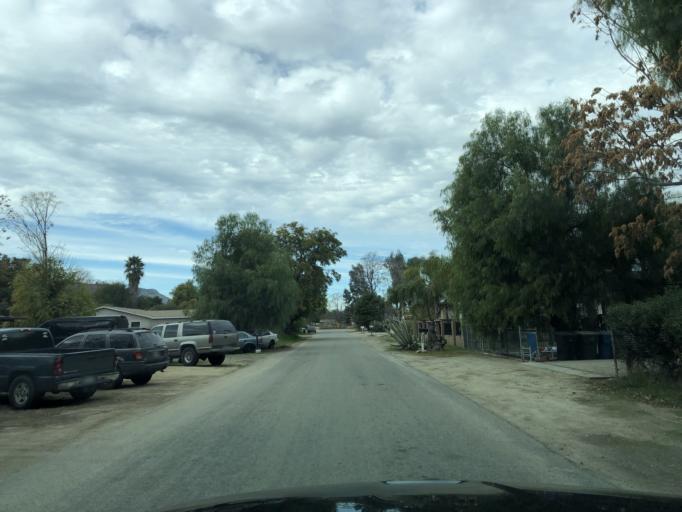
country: US
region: California
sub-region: Riverside County
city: Wildomar
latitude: 33.6016
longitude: -117.2779
